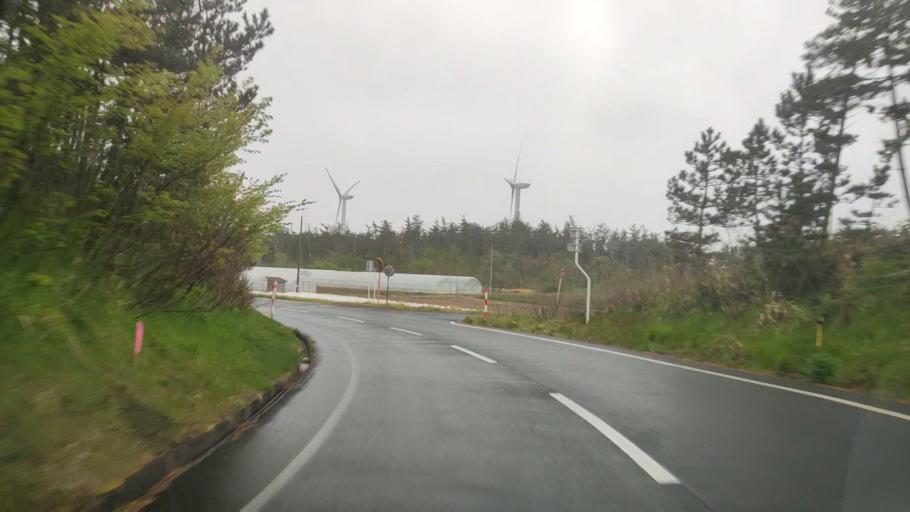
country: JP
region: Akita
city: Noshiromachi
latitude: 40.0941
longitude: 139.9629
